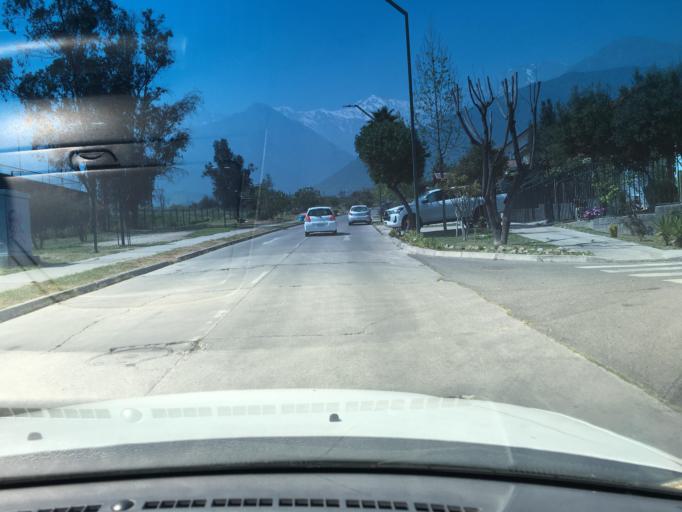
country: CL
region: Santiago Metropolitan
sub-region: Provincia de Santiago
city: Villa Presidente Frei, Nunoa, Santiago, Chile
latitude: -33.5109
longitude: -70.5315
